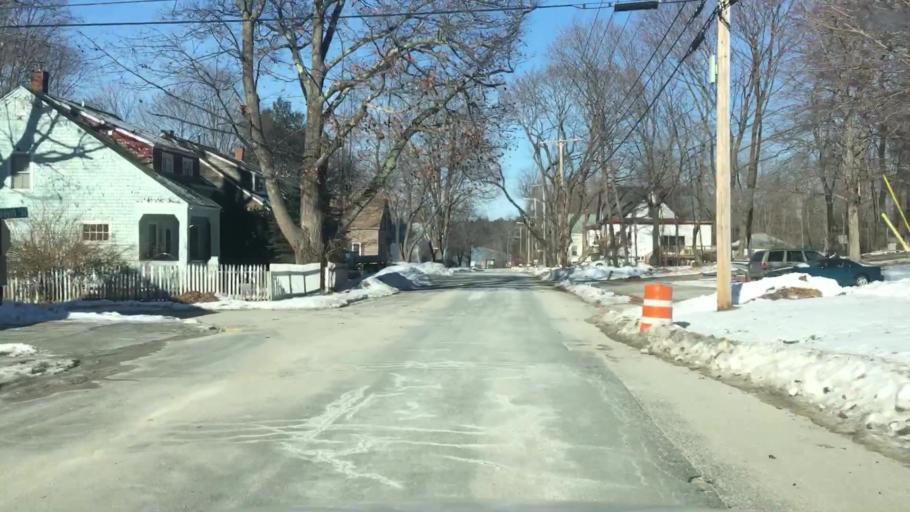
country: US
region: Maine
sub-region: Cumberland County
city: South Windham
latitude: 43.7342
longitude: -70.4206
